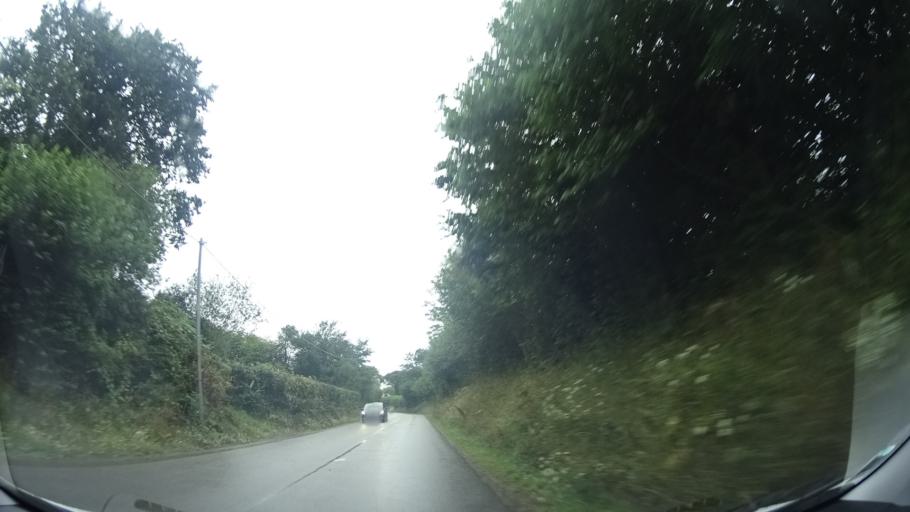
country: FR
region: Lower Normandy
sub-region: Departement de la Manche
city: Urville-Nacqueville
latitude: 49.5981
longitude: -1.7512
